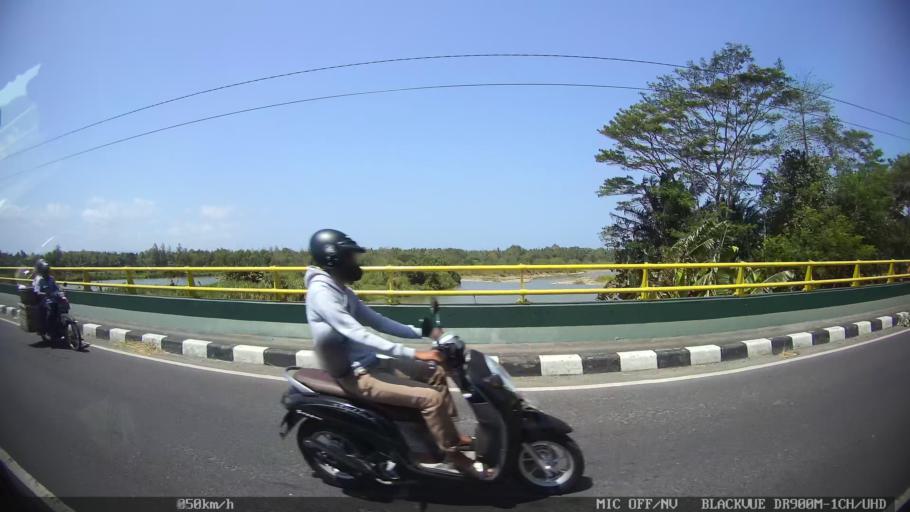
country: ID
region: Daerah Istimewa Yogyakarta
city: Srandakan
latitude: -7.9398
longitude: 110.2409
